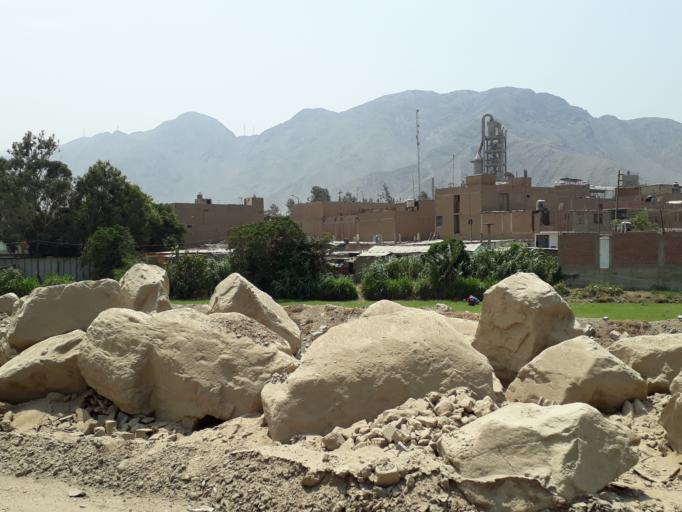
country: PE
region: Lima
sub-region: Lima
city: Santa Maria
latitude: -11.9893
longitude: -76.9028
